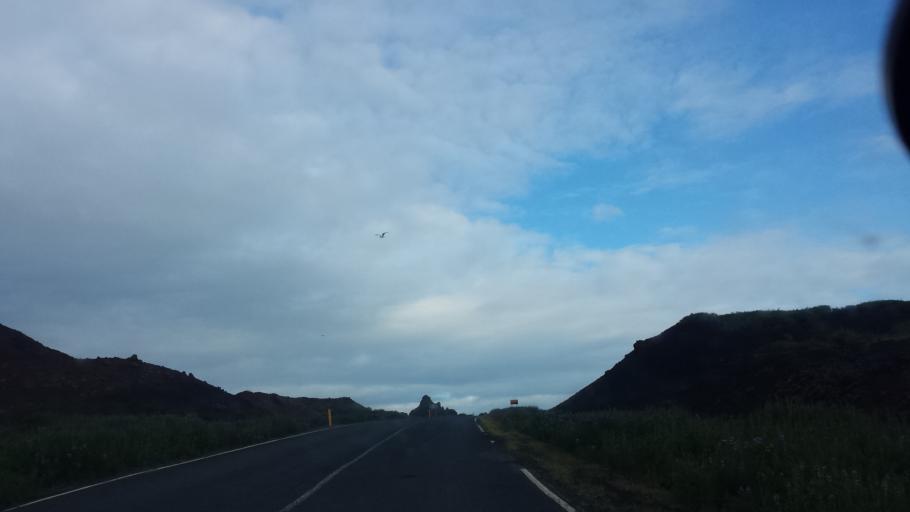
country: IS
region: South
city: Vestmannaeyjar
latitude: 63.4436
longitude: -20.2576
